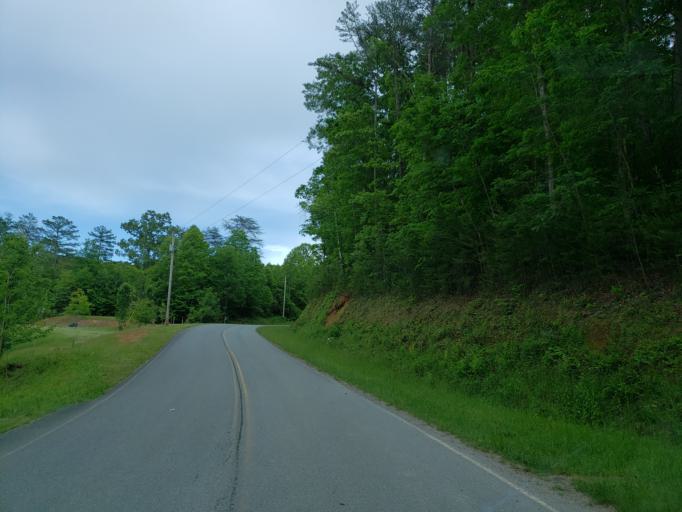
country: US
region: Georgia
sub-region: Fannin County
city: Blue Ridge
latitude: 34.8654
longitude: -84.3554
